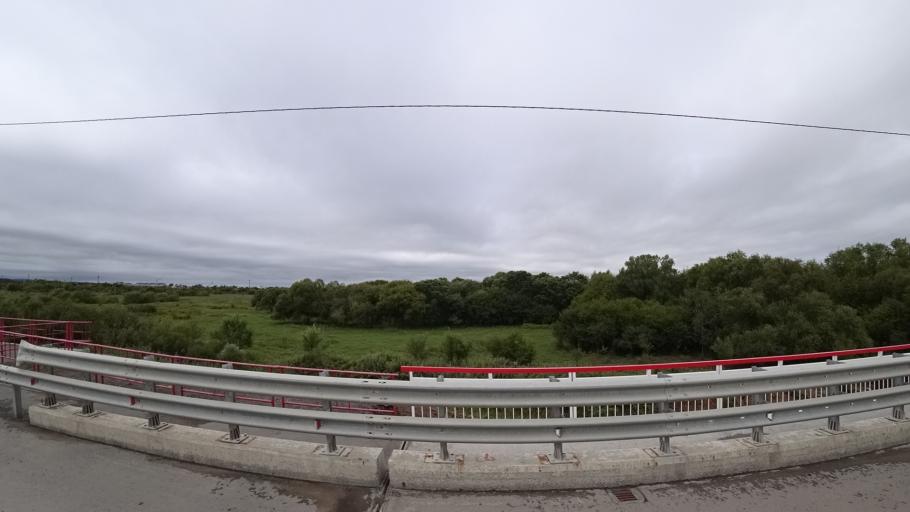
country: RU
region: Primorskiy
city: Monastyrishche
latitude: 44.1963
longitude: 132.4449
